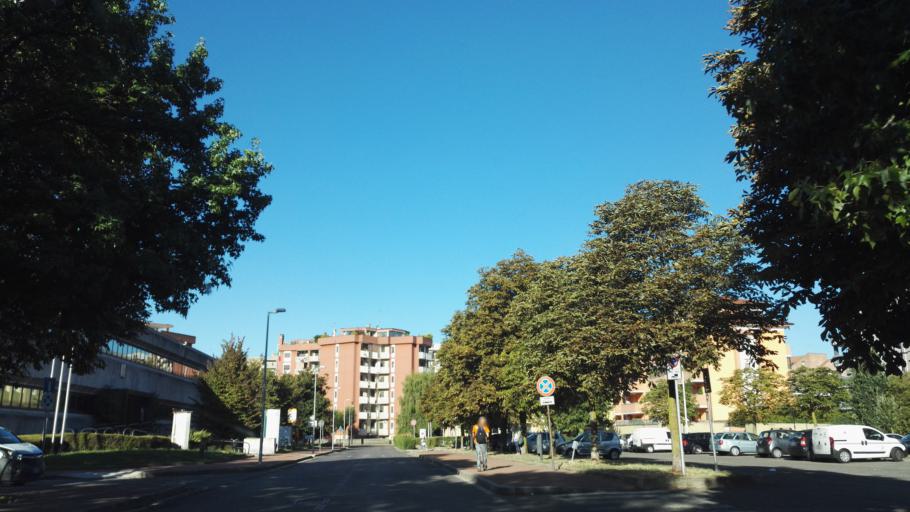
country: IT
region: Lombardy
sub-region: Citta metropolitana di Milano
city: San Giuliano Milanese
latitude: 45.4008
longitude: 9.2855
